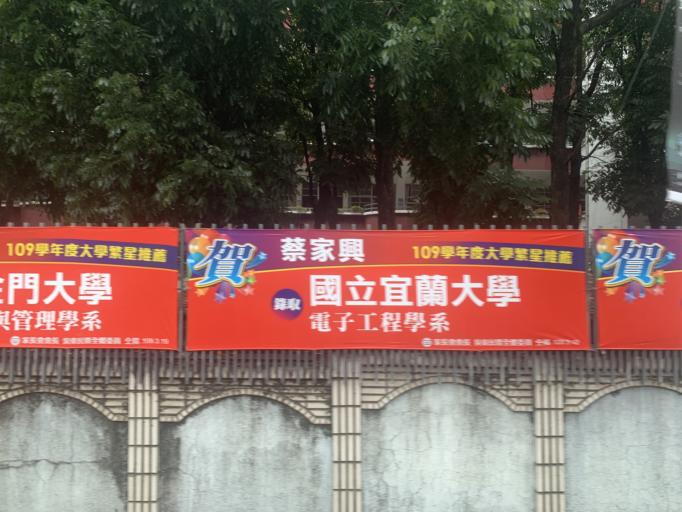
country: TW
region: Taiwan
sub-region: Chiayi
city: Jiayi Shi
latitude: 23.4892
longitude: 120.4645
